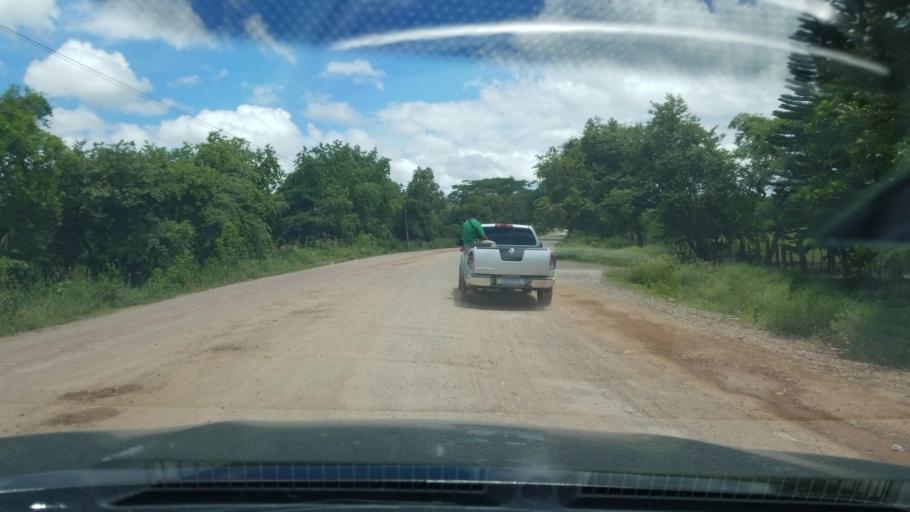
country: HN
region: Francisco Morazan
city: Talanga
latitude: 14.3737
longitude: -87.0617
